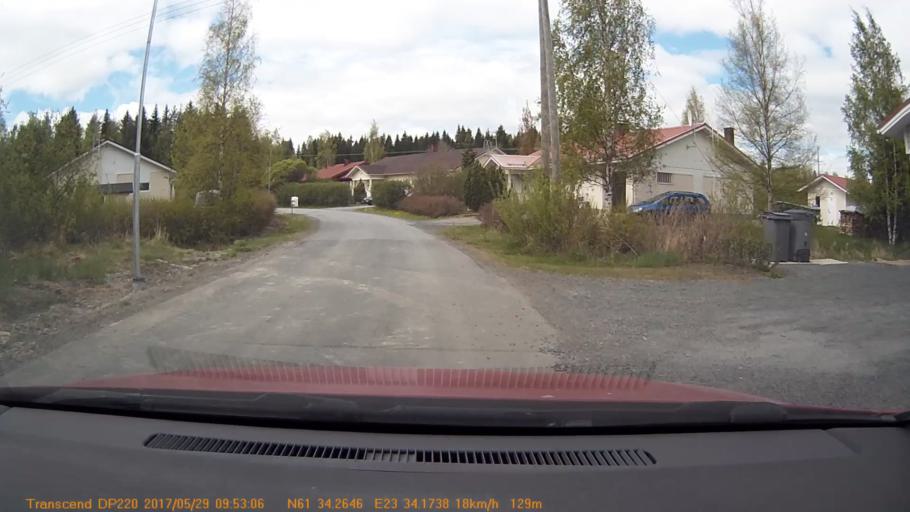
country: FI
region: Pirkanmaa
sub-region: Tampere
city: Yloejaervi
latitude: 61.5711
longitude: 23.5696
